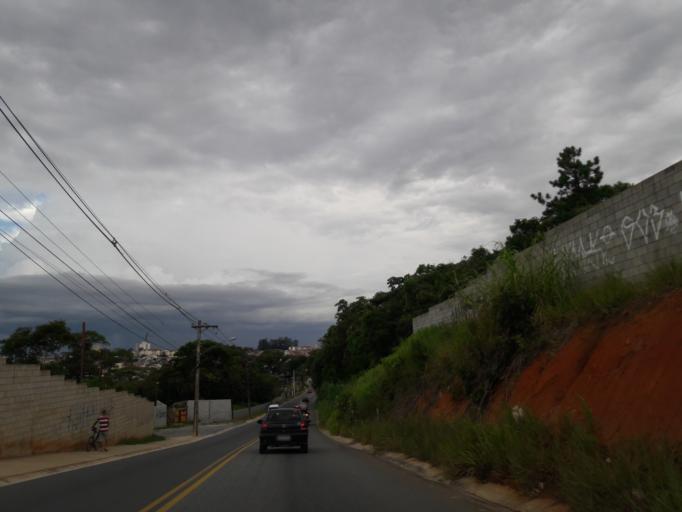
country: BR
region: Sao Paulo
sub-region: Aruja
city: Aruja
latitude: -23.3972
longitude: -46.4078
